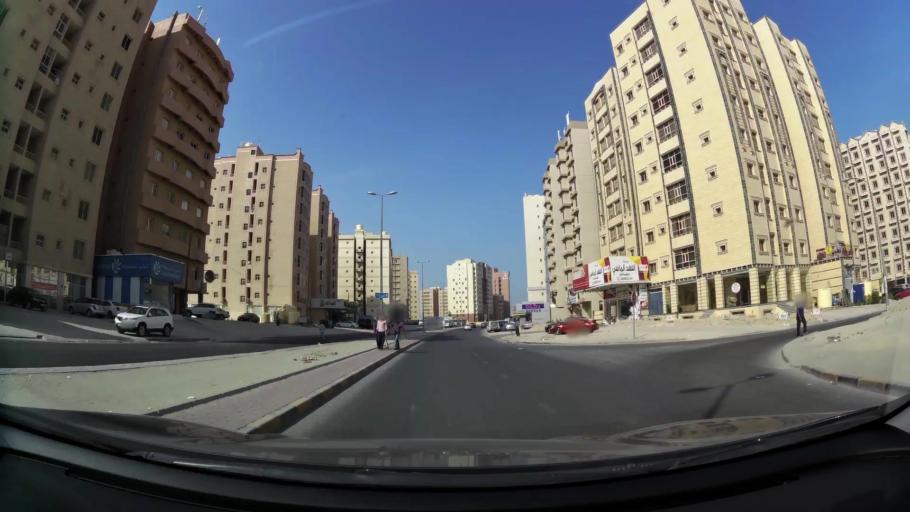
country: KW
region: Al Ahmadi
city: Al Mahbulah
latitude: 29.1555
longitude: 48.1159
